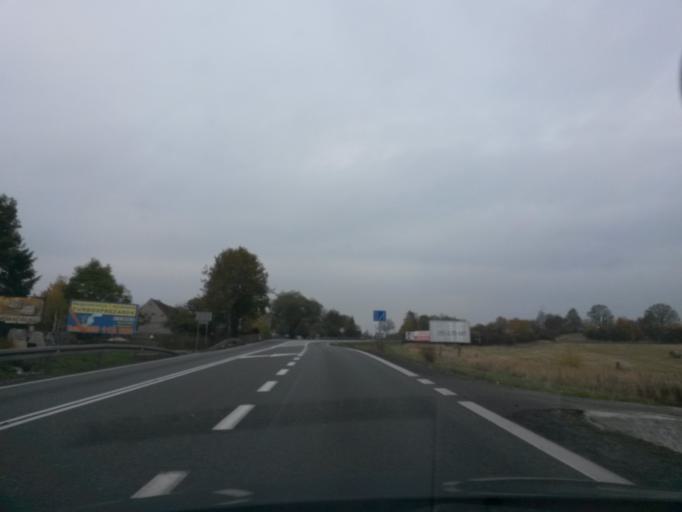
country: PL
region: Lower Silesian Voivodeship
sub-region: Powiat klodzki
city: Klodzko
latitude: 50.4631
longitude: 16.6812
